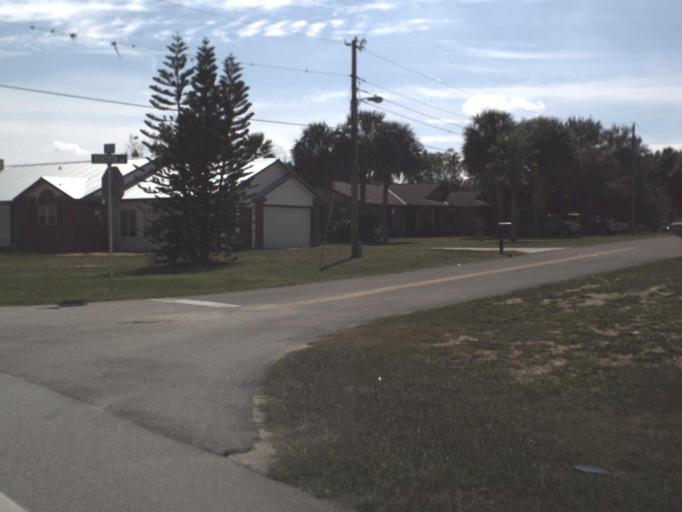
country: US
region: Florida
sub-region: Highlands County
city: Sebring
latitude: 27.5121
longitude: -81.4494
